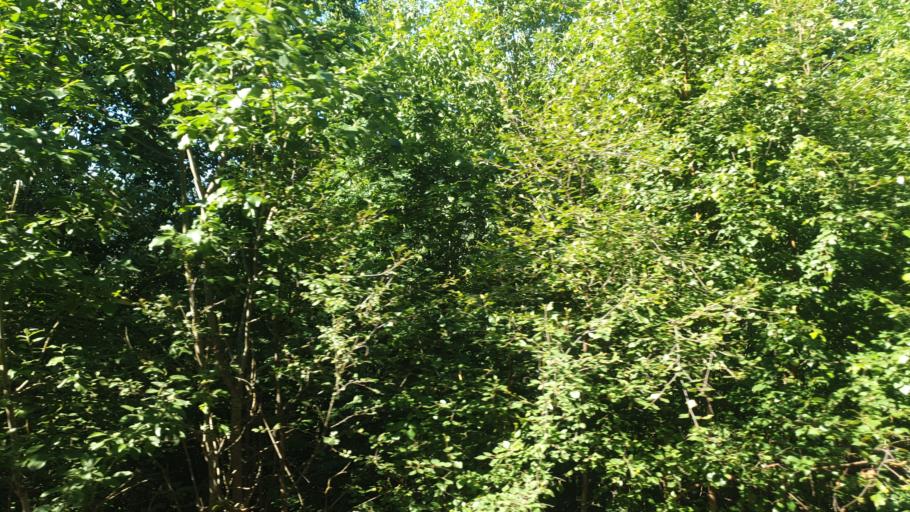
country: NO
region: Sor-Trondelag
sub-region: Meldal
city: Meldal
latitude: 63.1623
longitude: 9.7328
